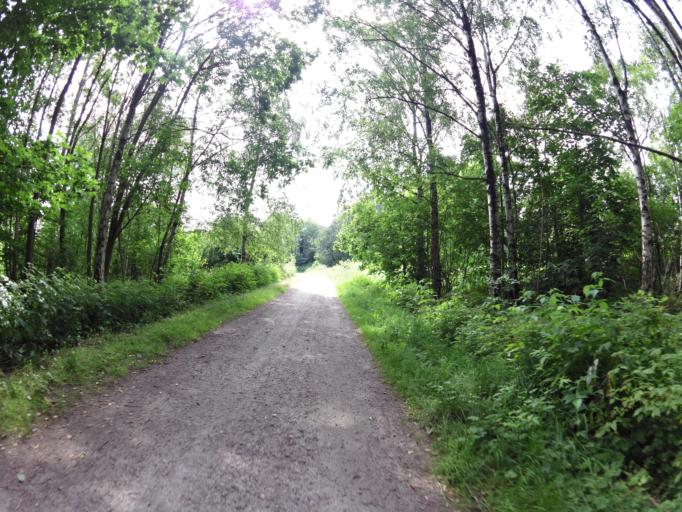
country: NO
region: Ostfold
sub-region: Fredrikstad
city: Fredrikstad
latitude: 59.2234
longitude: 10.9733
